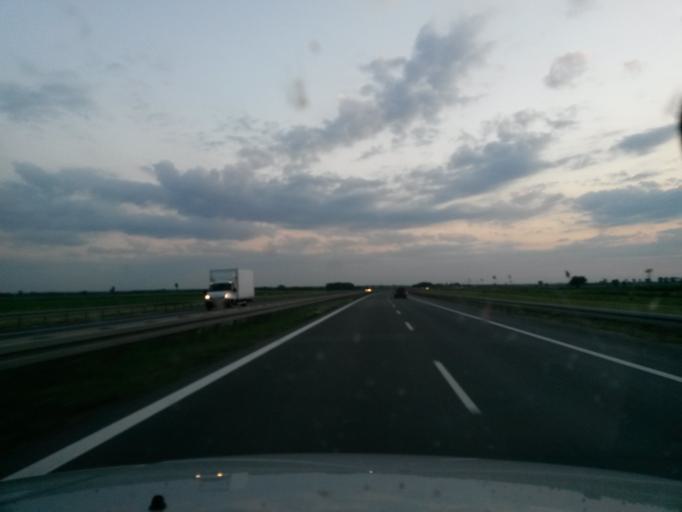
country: PL
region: Lower Silesian Voivodeship
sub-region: Powiat olesnicki
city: Dobroszyce
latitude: 51.2236
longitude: 17.3396
